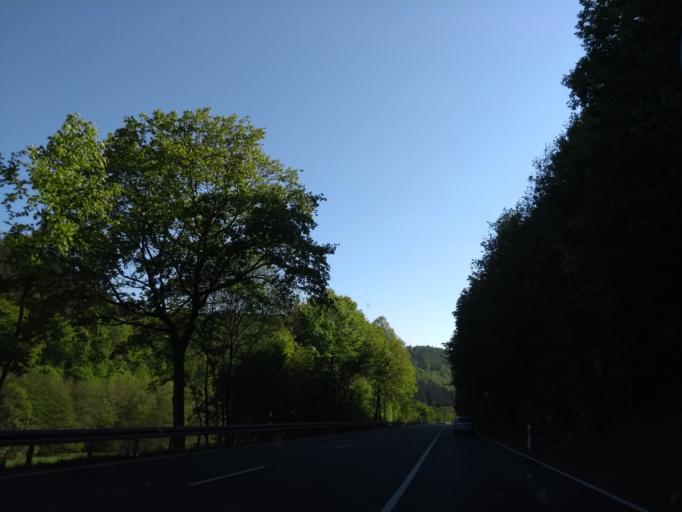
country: DE
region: Hesse
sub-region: Regierungsbezirk Giessen
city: Biedenkopf
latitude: 50.9366
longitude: 8.5362
